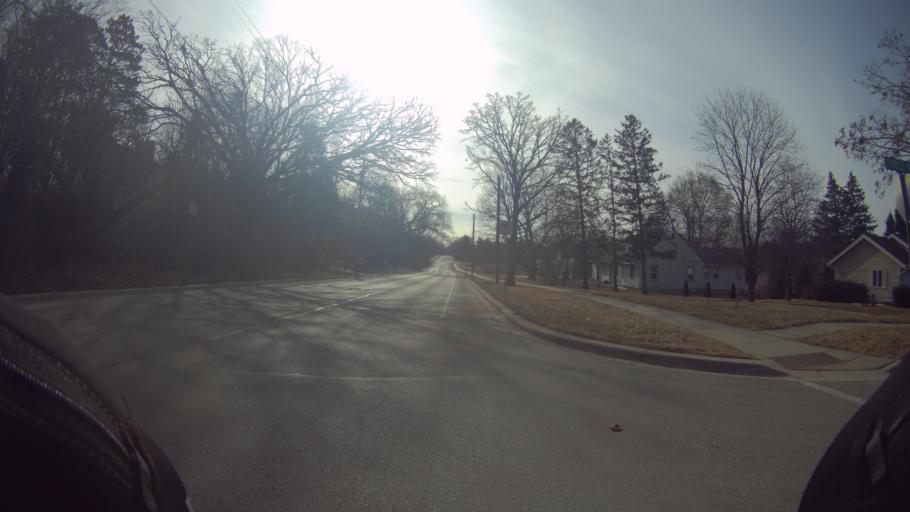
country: US
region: Wisconsin
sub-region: Dane County
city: Middleton
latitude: 43.0894
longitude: -89.4903
